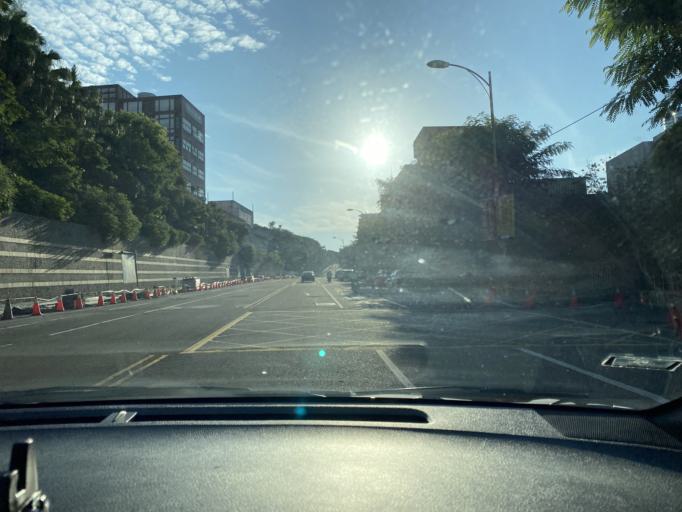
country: TW
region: Taiwan
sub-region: Changhua
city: Chang-hua
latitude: 24.0705
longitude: 120.5501
